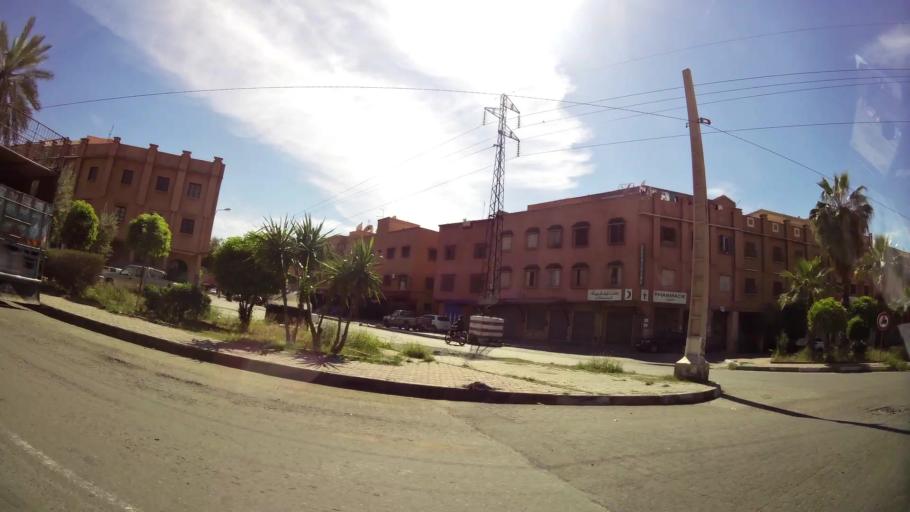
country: MA
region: Marrakech-Tensift-Al Haouz
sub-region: Marrakech
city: Marrakesh
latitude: 31.6381
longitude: -8.0434
